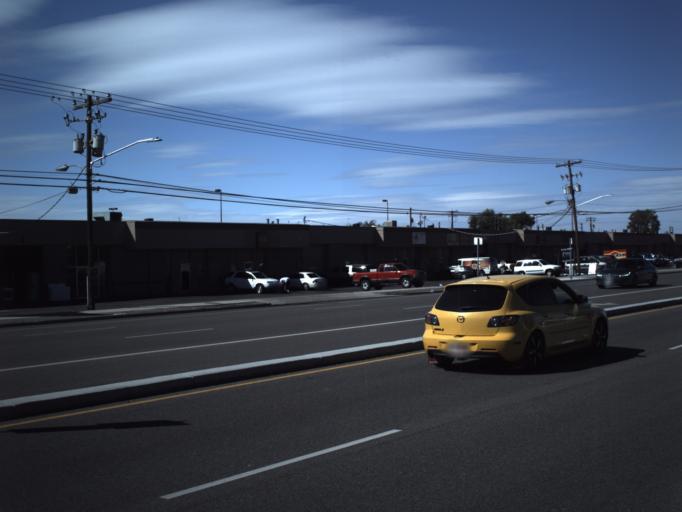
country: US
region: Utah
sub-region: Salt Lake County
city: South Salt Lake
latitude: 40.7307
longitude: -111.9389
